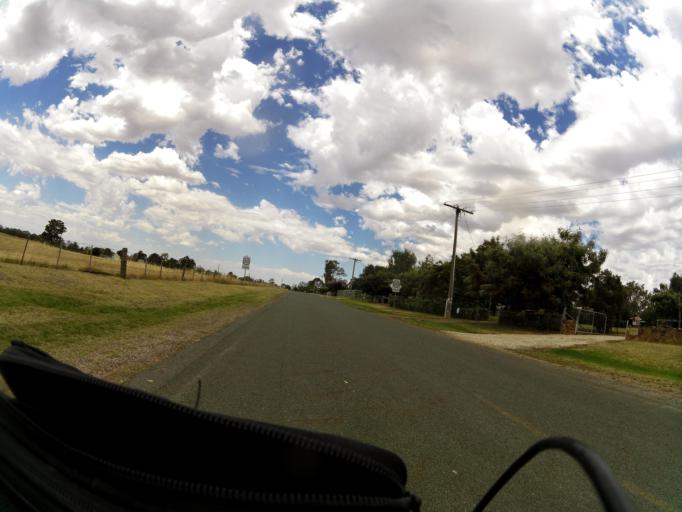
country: AU
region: Victoria
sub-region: Campaspe
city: Kyabram
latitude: -36.7424
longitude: 145.1355
